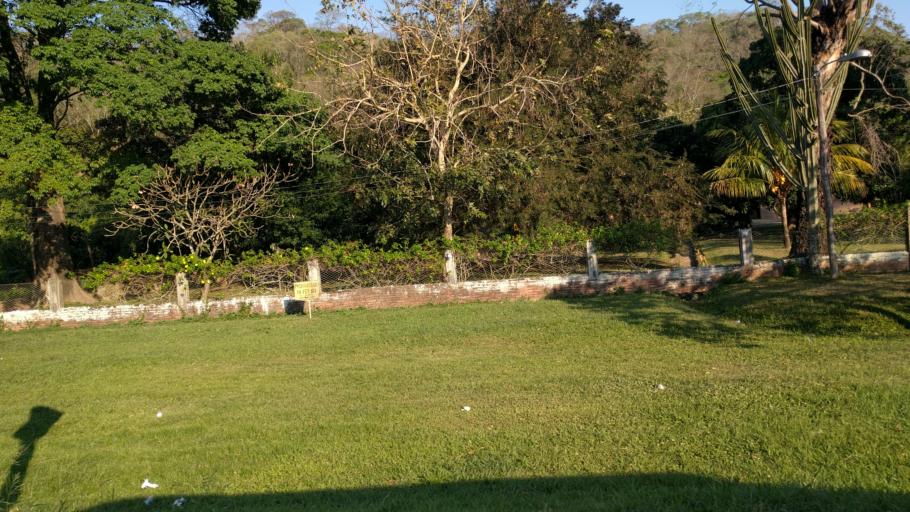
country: BO
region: Santa Cruz
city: Jorochito
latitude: -18.0718
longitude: -63.4416
